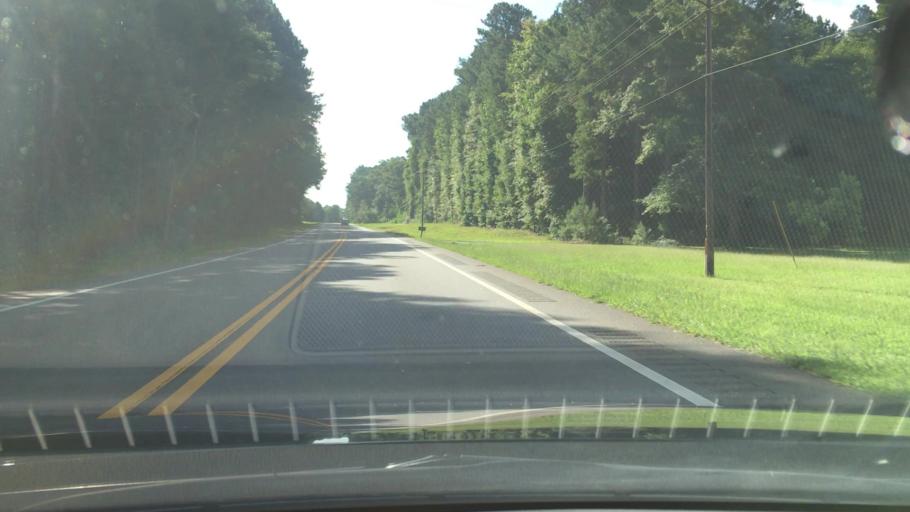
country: US
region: Georgia
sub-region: Morgan County
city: Madison
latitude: 33.5334
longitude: -83.4530
